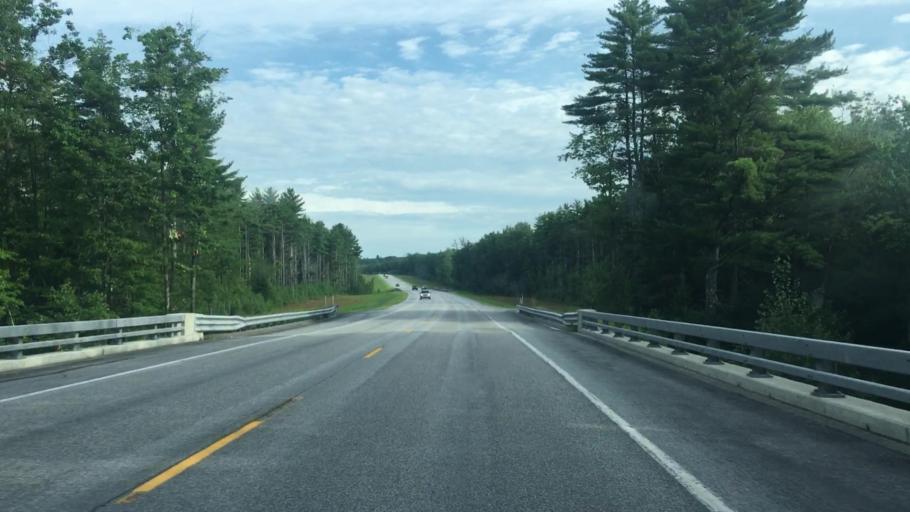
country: US
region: Maine
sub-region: Cumberland County
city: Gorham
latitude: 43.6575
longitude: -70.4491
